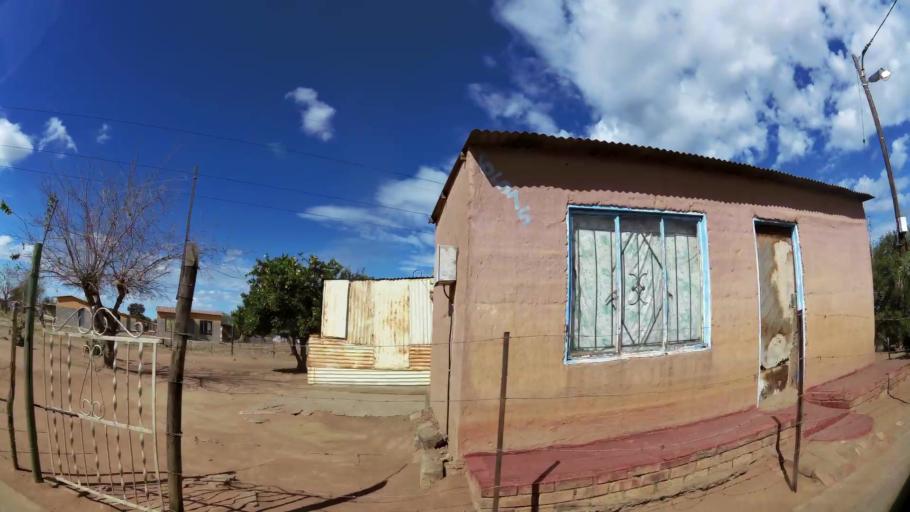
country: ZA
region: Limpopo
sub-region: Waterberg District Municipality
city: Bela-Bela
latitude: -24.8850
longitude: 28.3278
